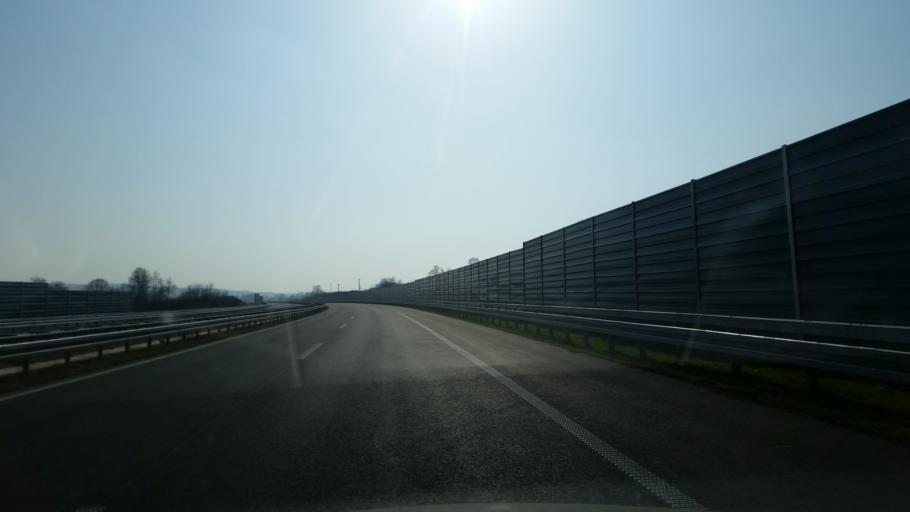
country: RS
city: Prislonica
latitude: 43.9631
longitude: 20.3963
